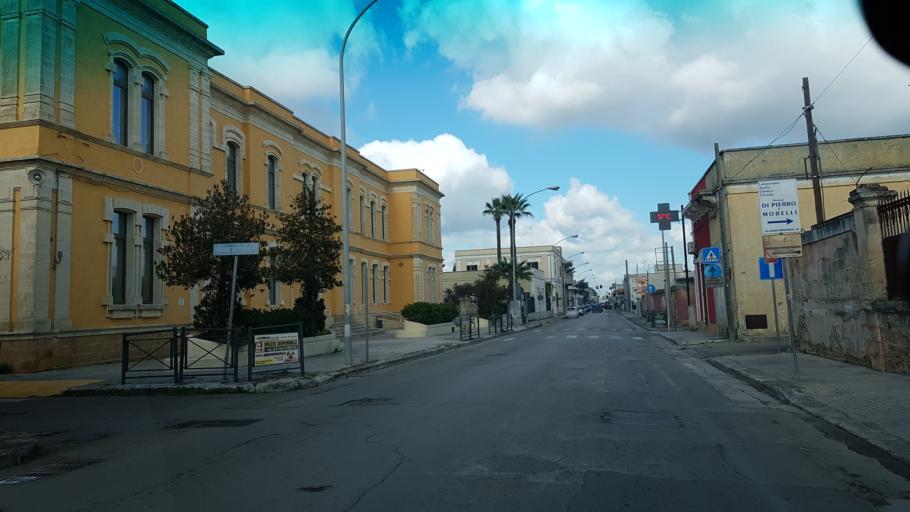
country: IT
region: Apulia
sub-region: Provincia di Lecce
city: Squinzano
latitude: 40.4335
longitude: 18.0419
